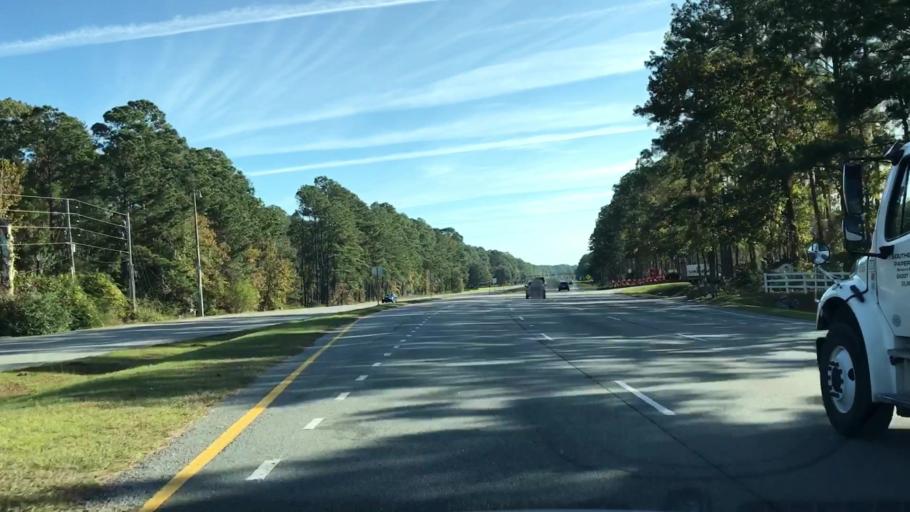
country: US
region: South Carolina
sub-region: Beaufort County
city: Bluffton
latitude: 32.2910
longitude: -80.9161
